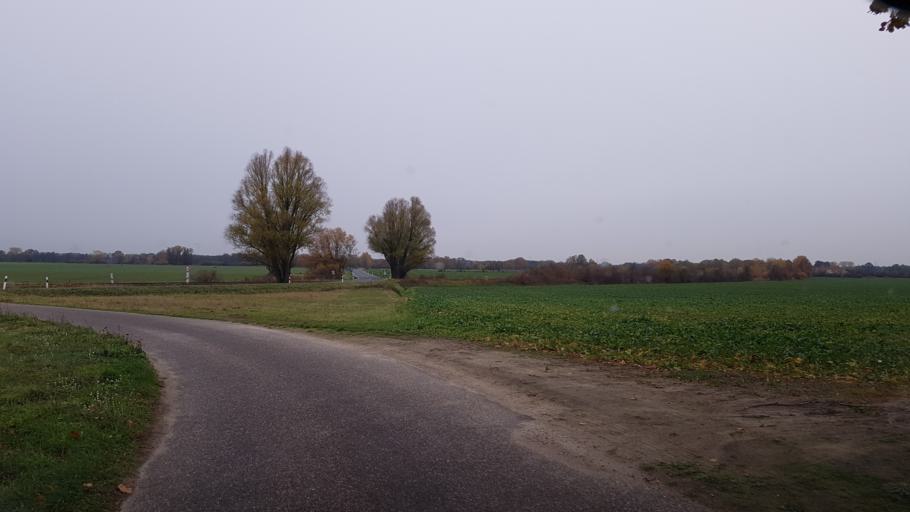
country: DE
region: Brandenburg
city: Finsterwalde
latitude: 51.6840
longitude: 13.7219
